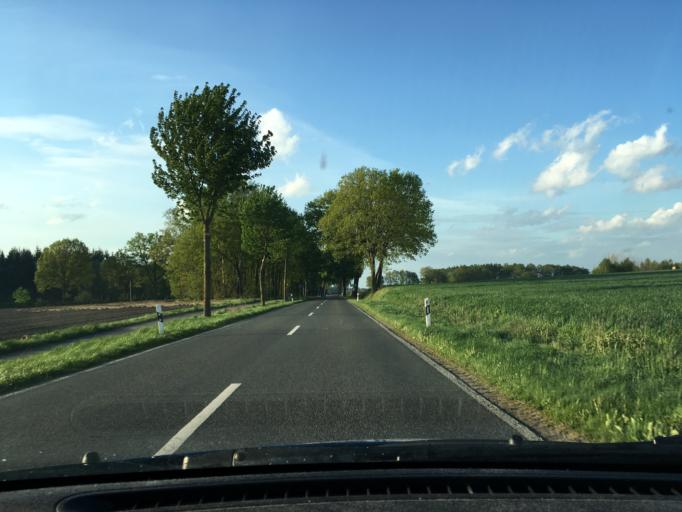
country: DE
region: Lower Saxony
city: Wietzendorf
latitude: 52.8896
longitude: 9.9835
